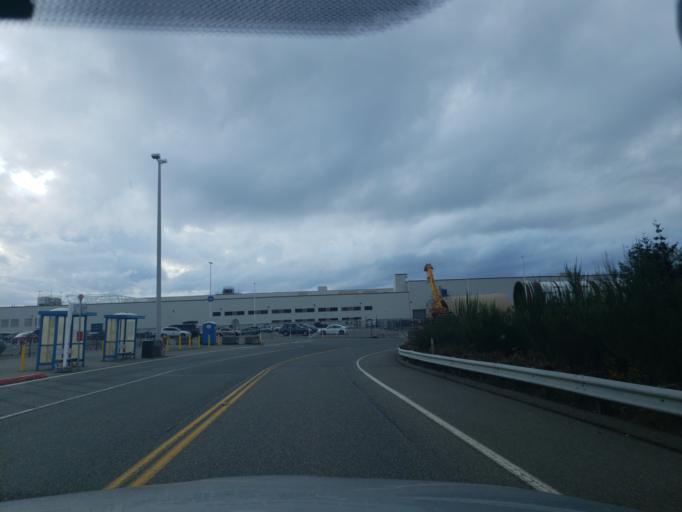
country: US
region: Washington
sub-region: Snohomish County
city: Mukilteo
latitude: 47.9324
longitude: -122.2776
